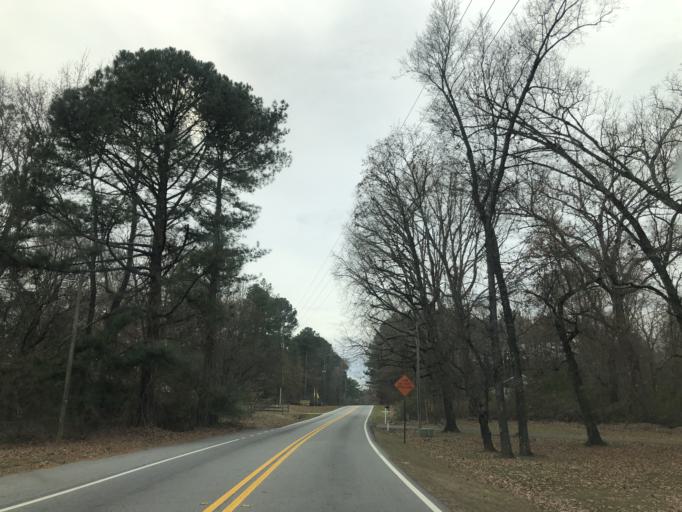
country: US
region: Georgia
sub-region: Henry County
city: Stockbridge
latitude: 33.6339
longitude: -84.2143
